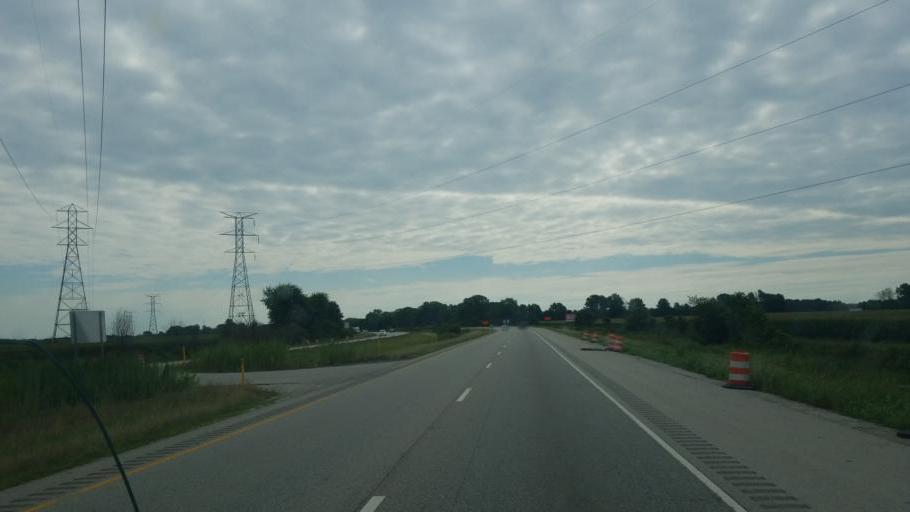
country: US
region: Indiana
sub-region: Vigo County
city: Seelyville
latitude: 39.4298
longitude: -87.3071
